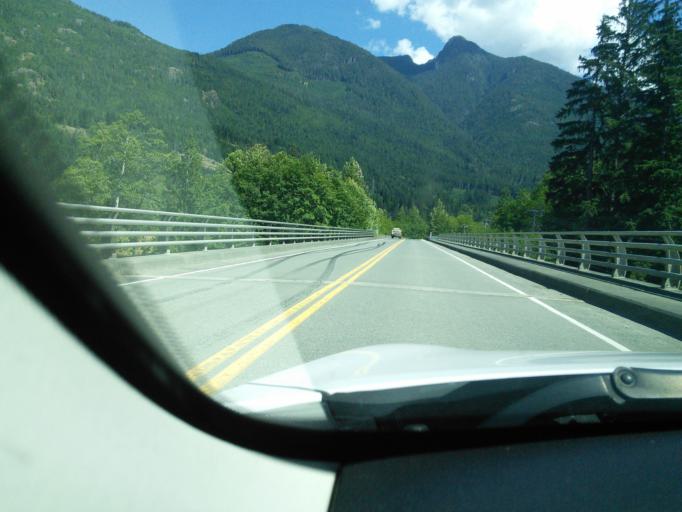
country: CA
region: British Columbia
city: Campbell River
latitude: 50.3613
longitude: -125.9190
